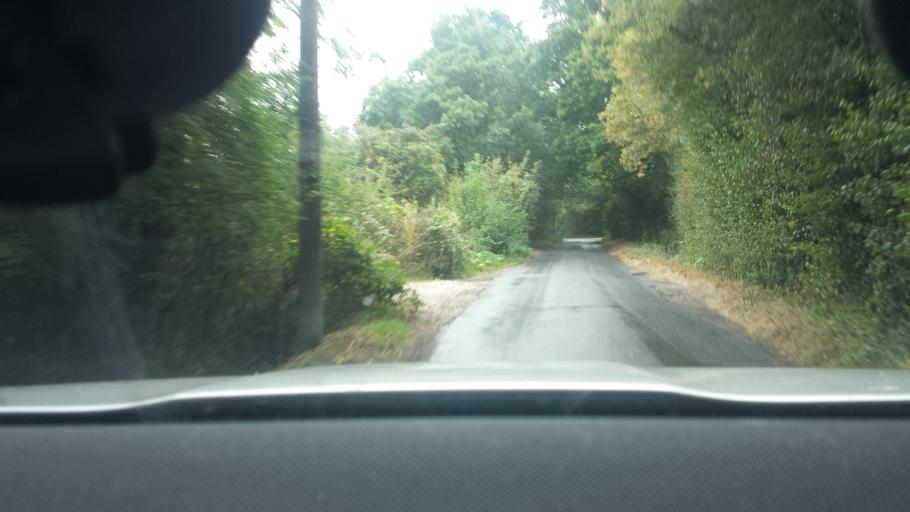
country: GB
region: England
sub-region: Kent
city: Staplehurst
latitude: 51.1772
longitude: 0.5440
